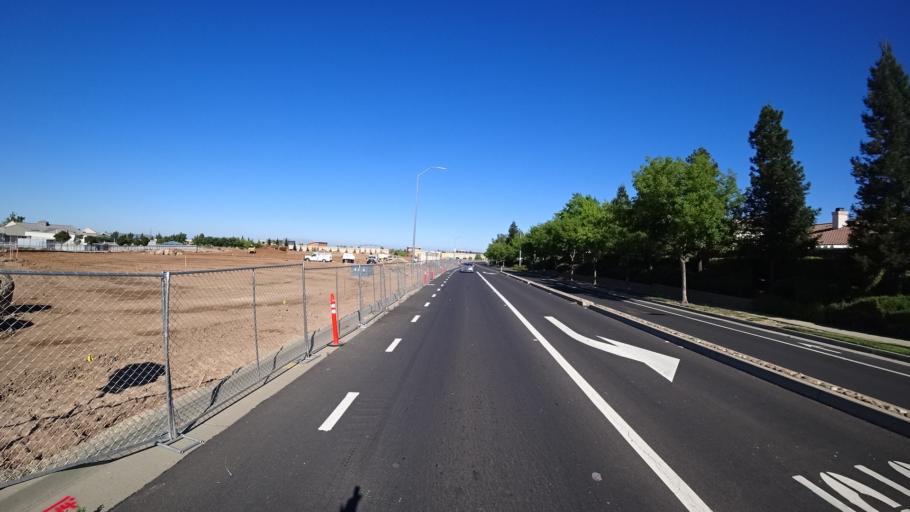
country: US
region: California
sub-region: Placer County
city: Rocklin
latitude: 38.7901
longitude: -121.2748
